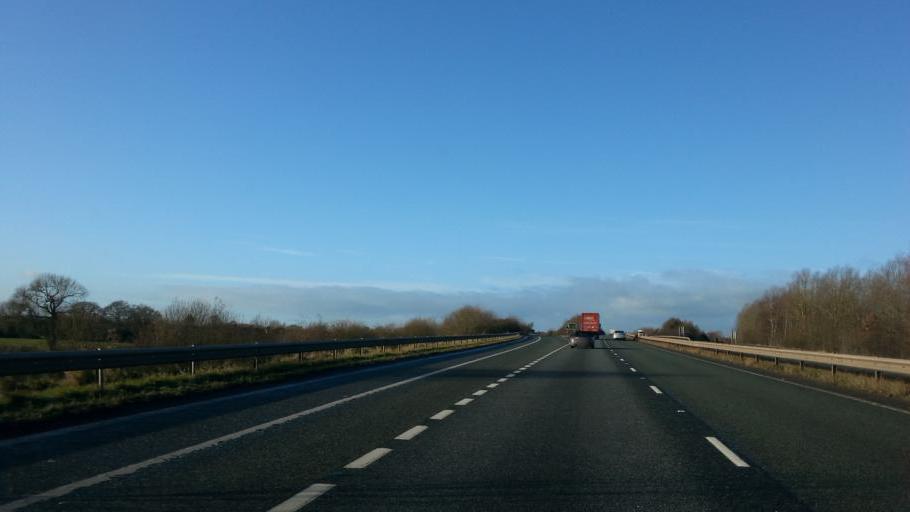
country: GB
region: England
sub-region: Derbyshire
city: Etwall
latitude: 52.8759
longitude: -1.6164
